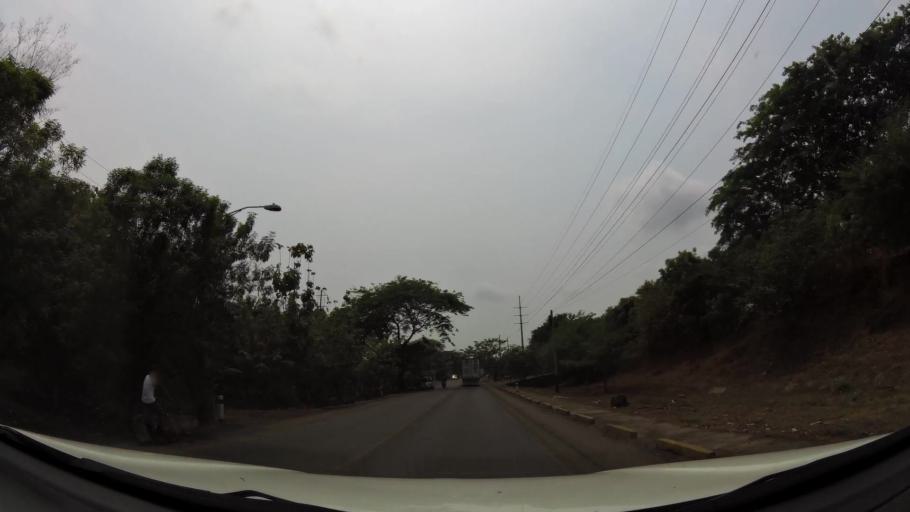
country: NI
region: Chinandega
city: Chinandega
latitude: 12.6386
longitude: -87.1258
